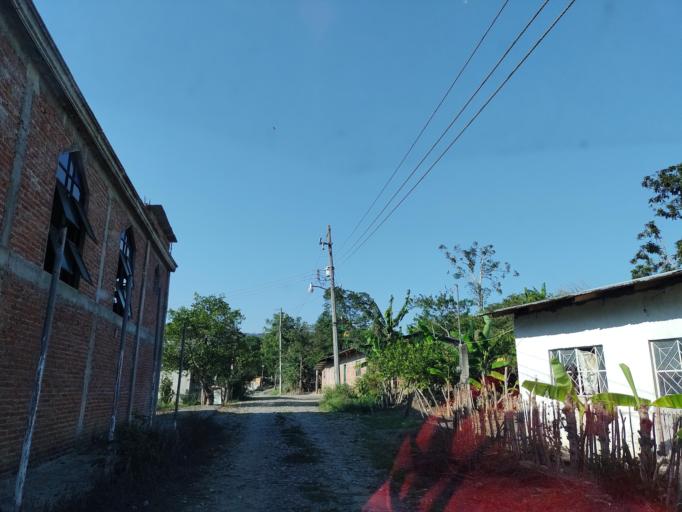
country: MX
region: Veracruz
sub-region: Papantla
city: Polutla
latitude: 20.4554
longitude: -97.2258
